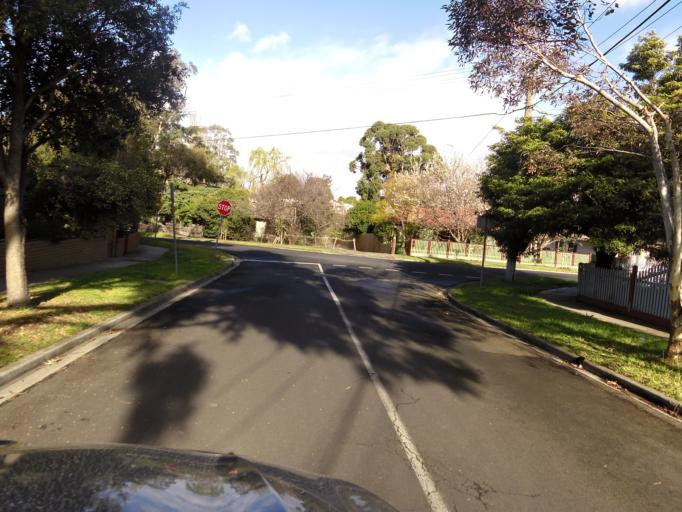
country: AU
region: Victoria
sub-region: Maribyrnong
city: Kingsville
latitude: -37.8089
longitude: 144.8684
